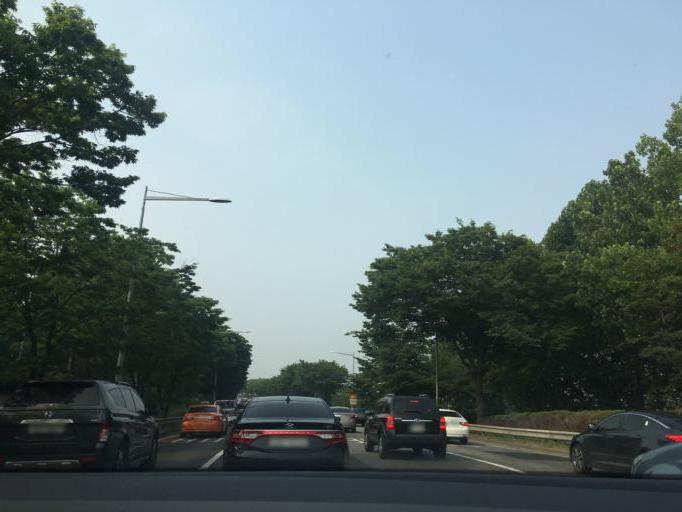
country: KR
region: Gyeonggi-do
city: Guri-si
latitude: 37.5588
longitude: 127.1264
